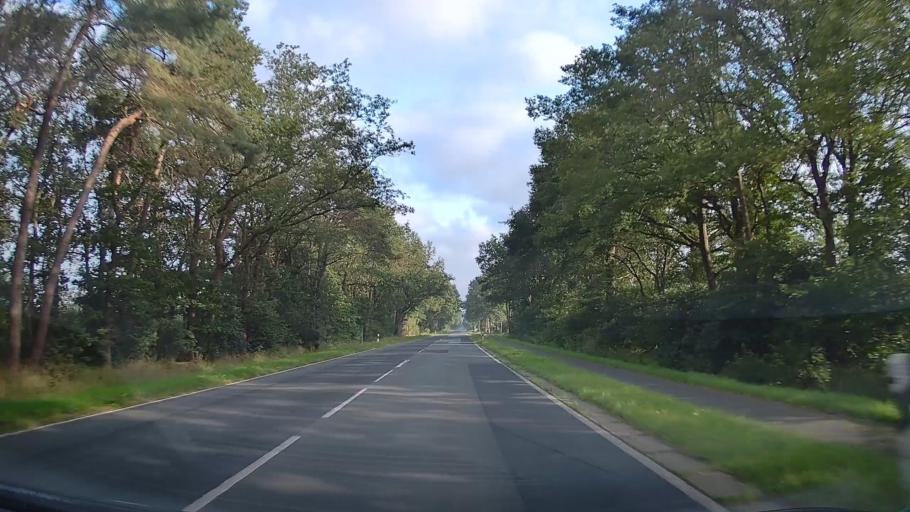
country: DE
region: Lower Saxony
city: Wardenburg
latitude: 53.0088
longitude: 8.1957
